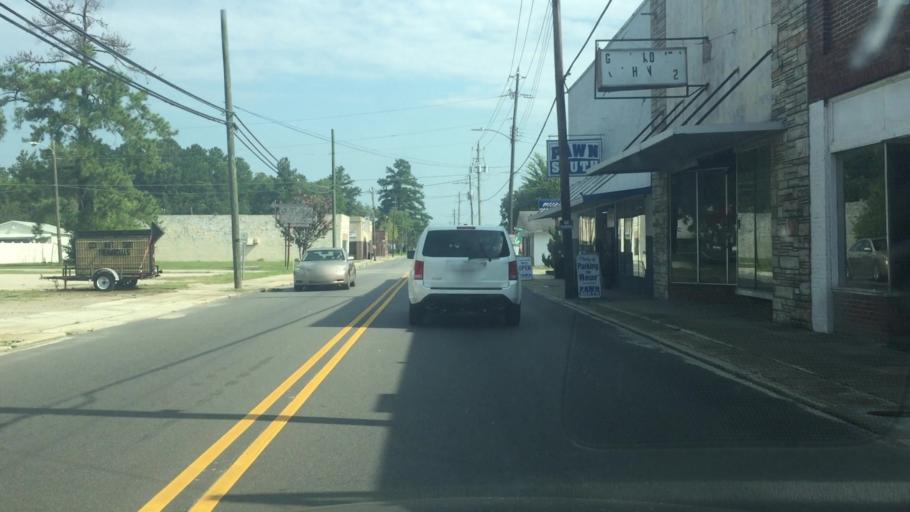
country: US
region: North Carolina
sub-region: Columbus County
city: Chadbourn
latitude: 34.3240
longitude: -78.8264
